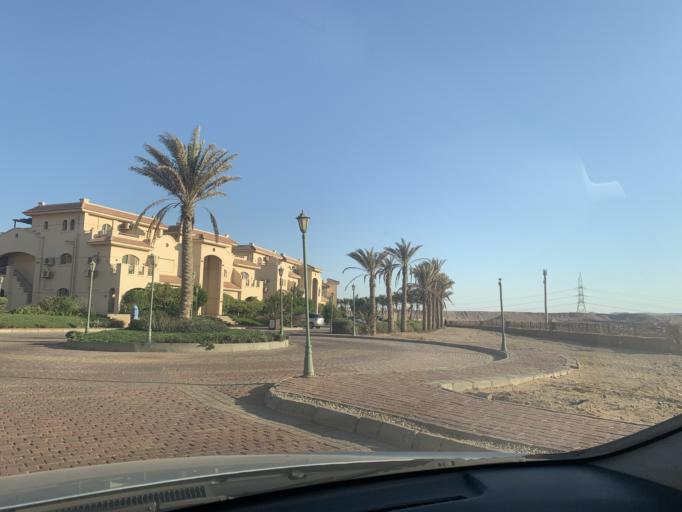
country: EG
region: As Suways
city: Ain Sukhna
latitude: 29.3741
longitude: 32.5687
